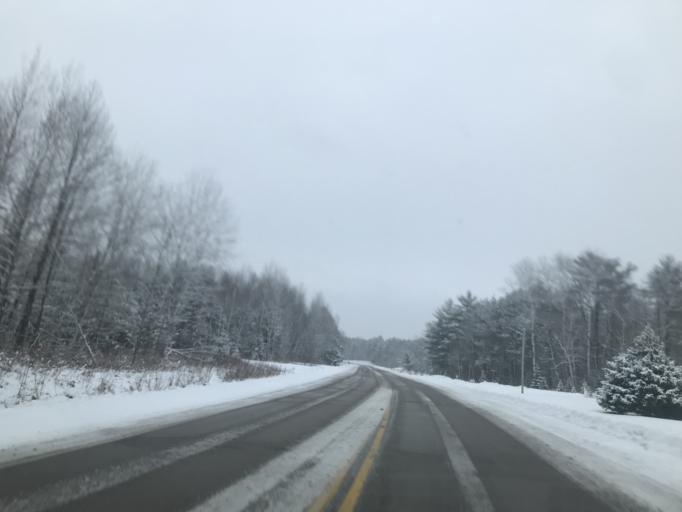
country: US
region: Wisconsin
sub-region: Oconto County
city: Oconto Falls
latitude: 44.8579
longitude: -88.0822
